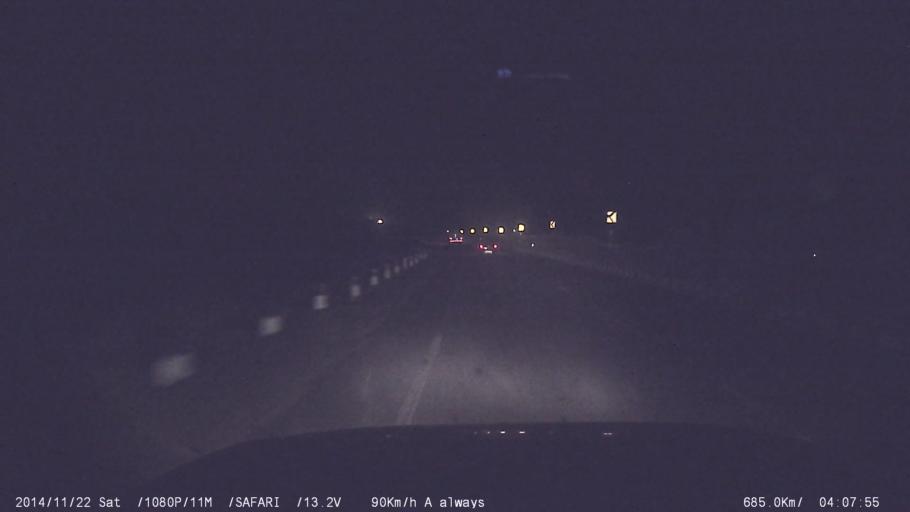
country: IN
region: Tamil Nadu
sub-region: Erode
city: Perundurai
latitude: 11.2847
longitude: 77.5589
